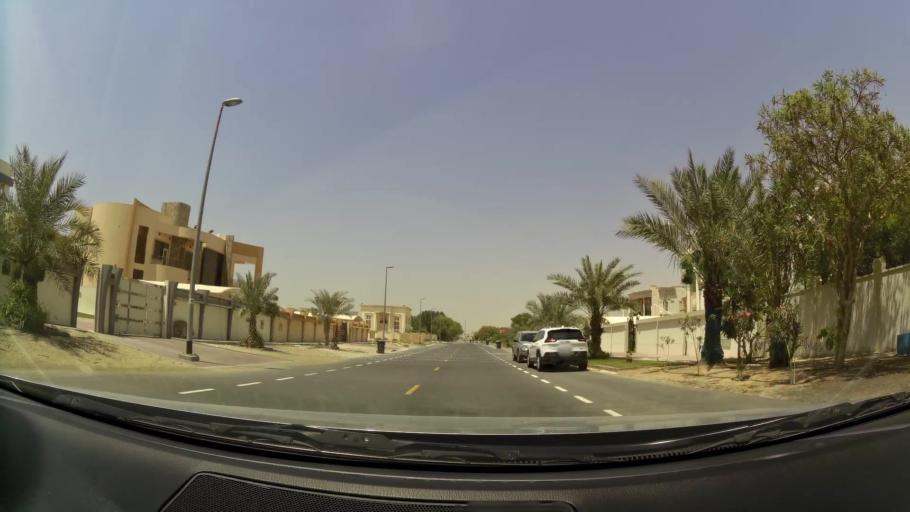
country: AE
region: Dubai
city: Dubai
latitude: 25.0910
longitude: 55.2162
